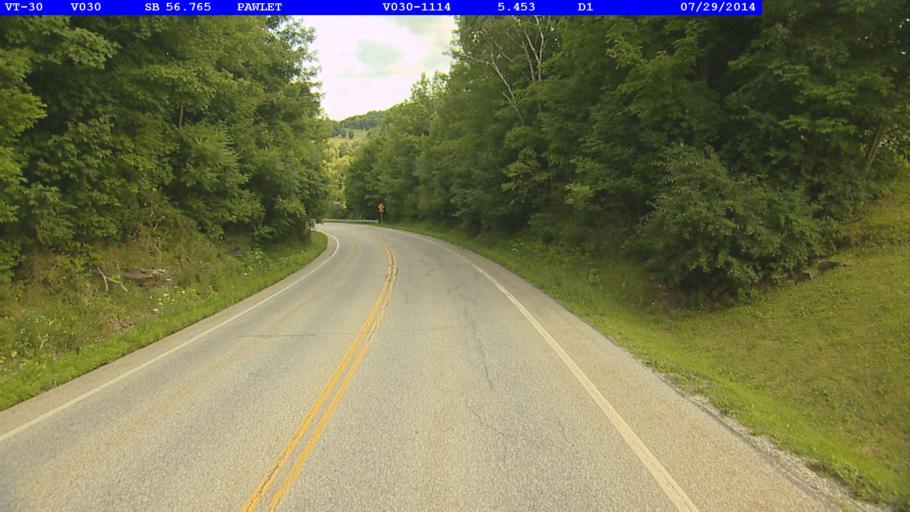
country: US
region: New York
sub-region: Washington County
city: Granville
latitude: 43.3762
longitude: -73.2043
